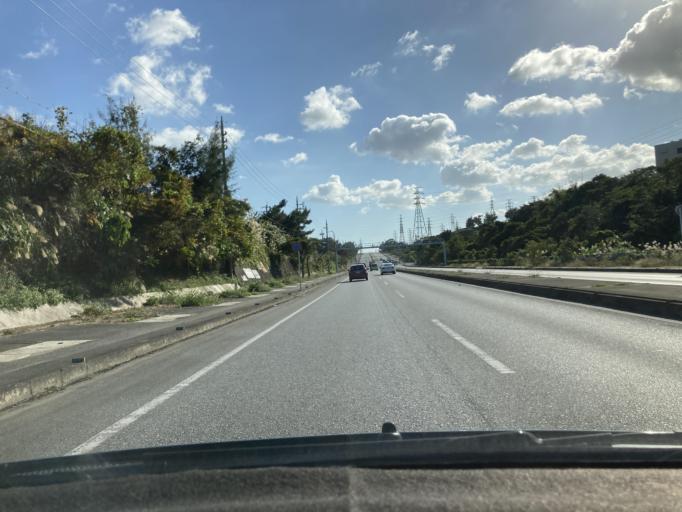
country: JP
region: Okinawa
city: Ishikawa
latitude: 26.3988
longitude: 127.8291
